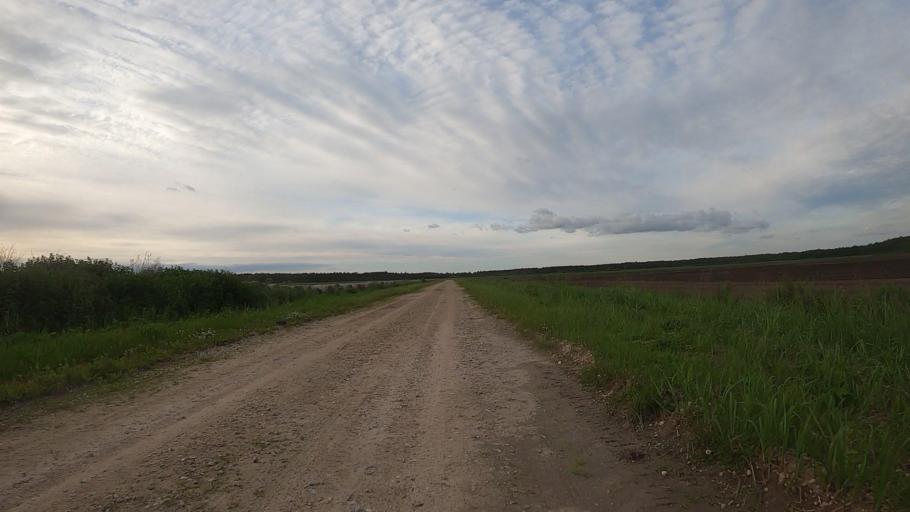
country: LV
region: Olaine
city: Olaine
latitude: 56.8189
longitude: 23.9517
